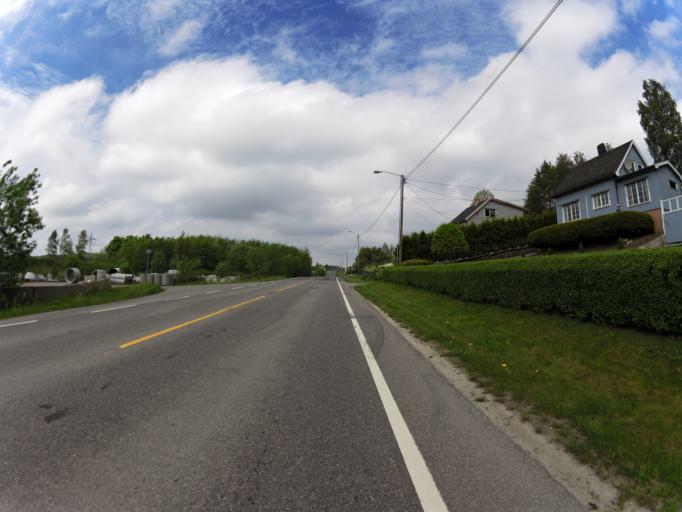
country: NO
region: Ostfold
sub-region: Rade
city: Karlshus
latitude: 59.3387
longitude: 10.9342
